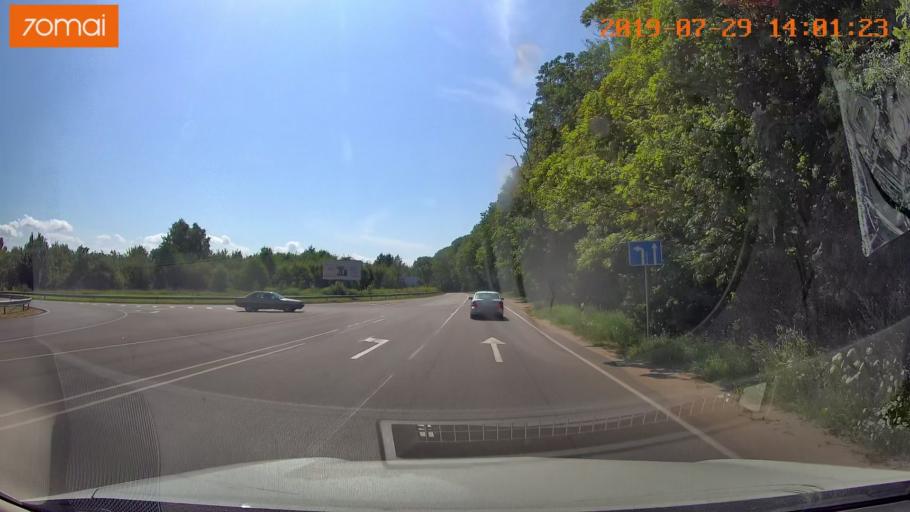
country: RU
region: Kaliningrad
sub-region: Gorod Kaliningrad
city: Baltiysk
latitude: 54.6709
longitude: 19.9221
